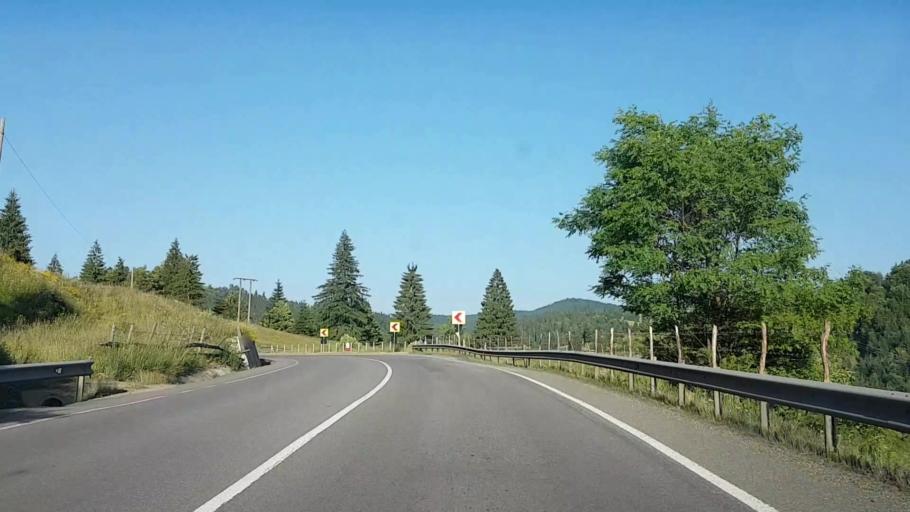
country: RO
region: Bistrita-Nasaud
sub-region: Comuna Tiha Bargaului
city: Tureac
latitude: 47.2217
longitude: 24.9512
